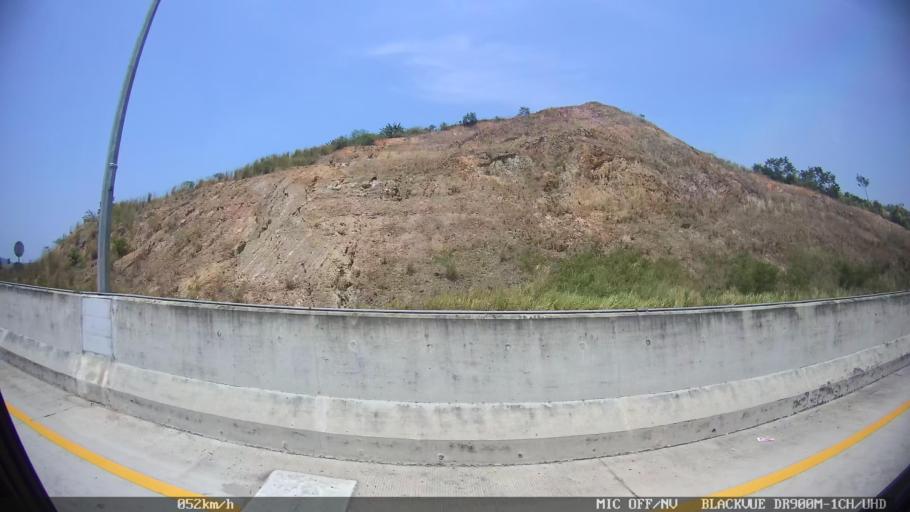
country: ID
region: Lampung
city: Panjang
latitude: -5.4037
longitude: 105.3461
